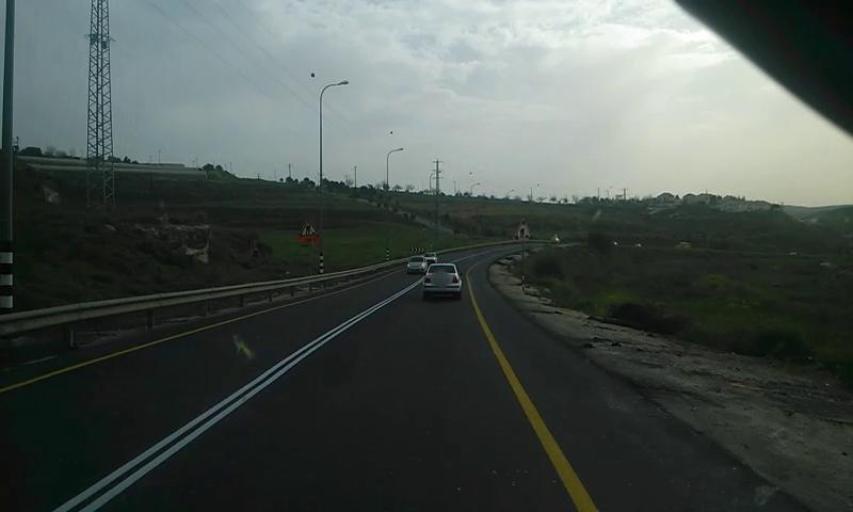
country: PS
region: West Bank
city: Jit
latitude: 32.2101
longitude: 35.1637
